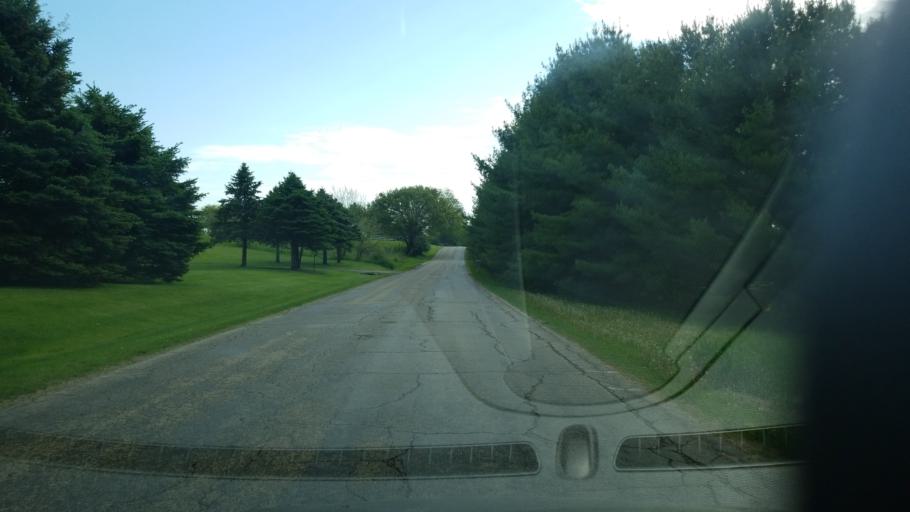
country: US
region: Wisconsin
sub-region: Dane County
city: Oregon
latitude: 42.9137
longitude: -89.3538
